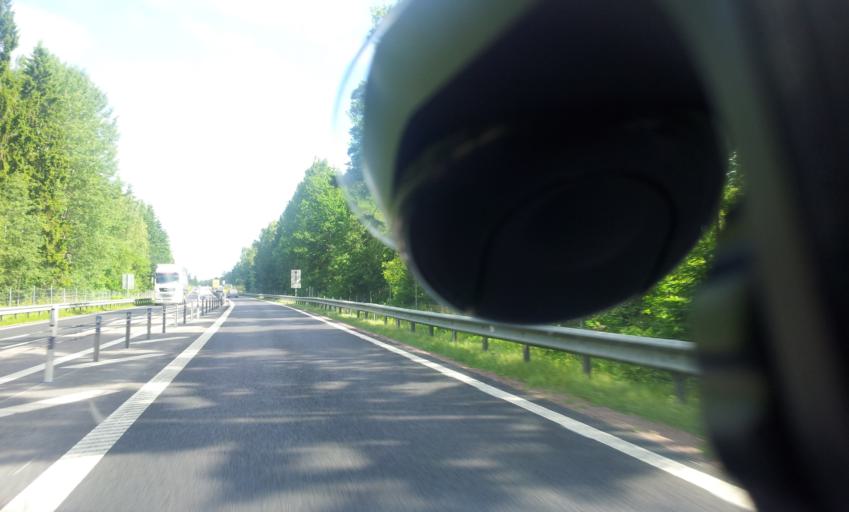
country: SE
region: Kalmar
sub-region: Monsteras Kommun
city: Timmernabben
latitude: 56.8694
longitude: 16.3823
